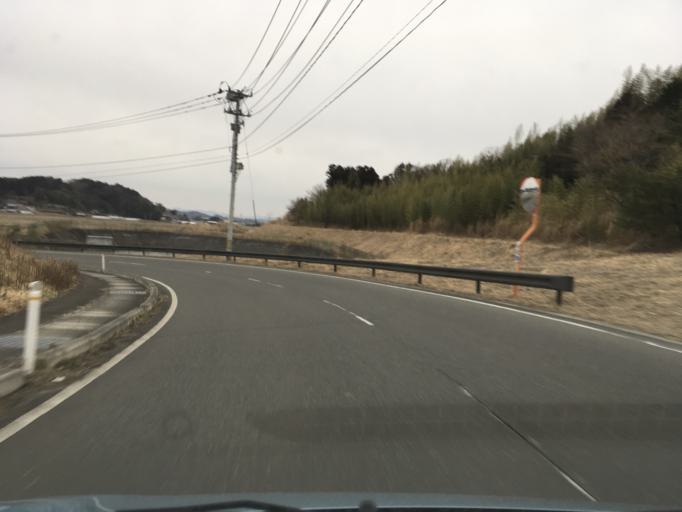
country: JP
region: Miyagi
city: Wakuya
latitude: 38.7021
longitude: 141.1708
